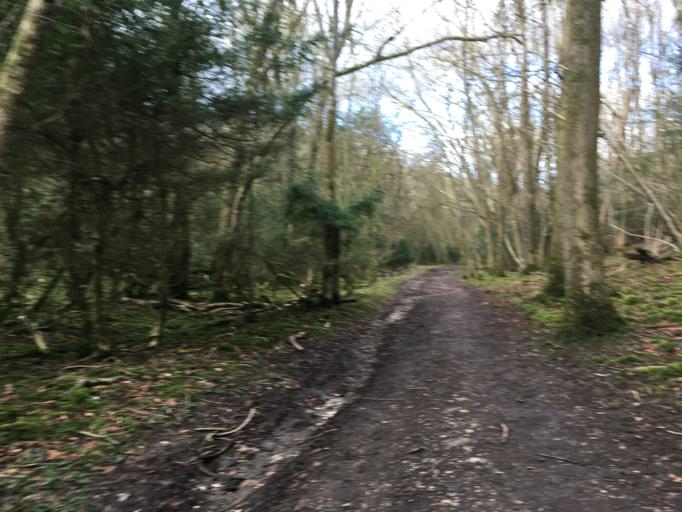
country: GB
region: England
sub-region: Surrey
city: Mickleham
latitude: 51.2528
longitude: -0.3061
